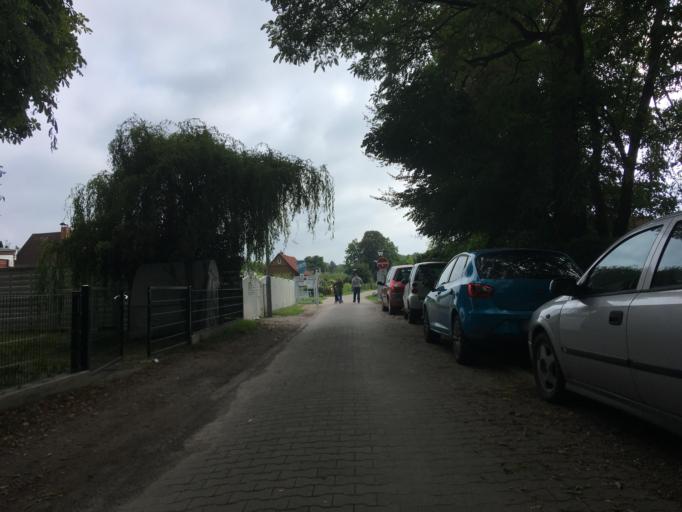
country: DE
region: Berlin
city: Konradshohe
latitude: 52.6053
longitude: 13.2211
